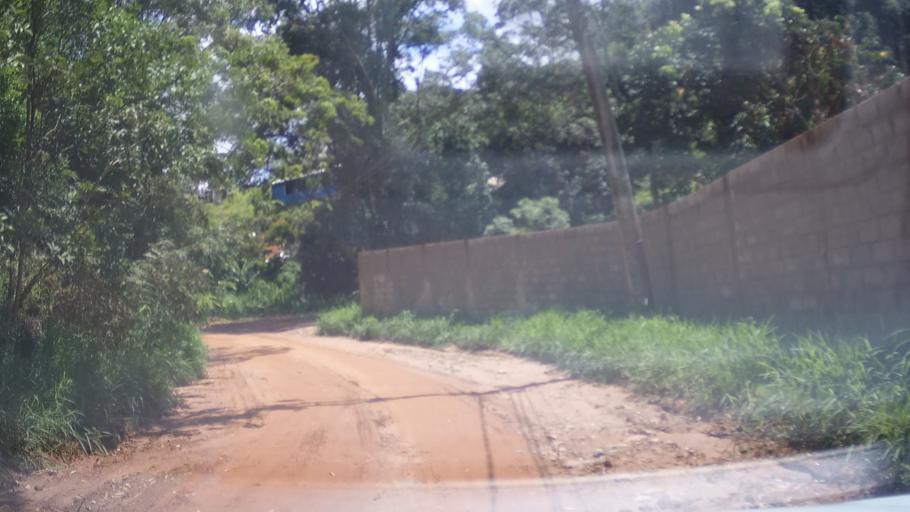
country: BR
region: Sao Paulo
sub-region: Campo Limpo Paulista
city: Campo Limpo Paulista
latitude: -23.2036
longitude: -46.7216
